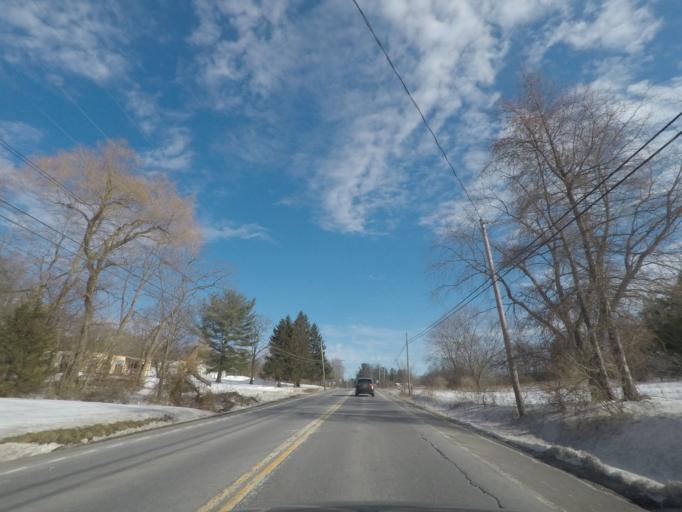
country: US
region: New York
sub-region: Albany County
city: Altamont
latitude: 42.7790
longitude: -74.0565
